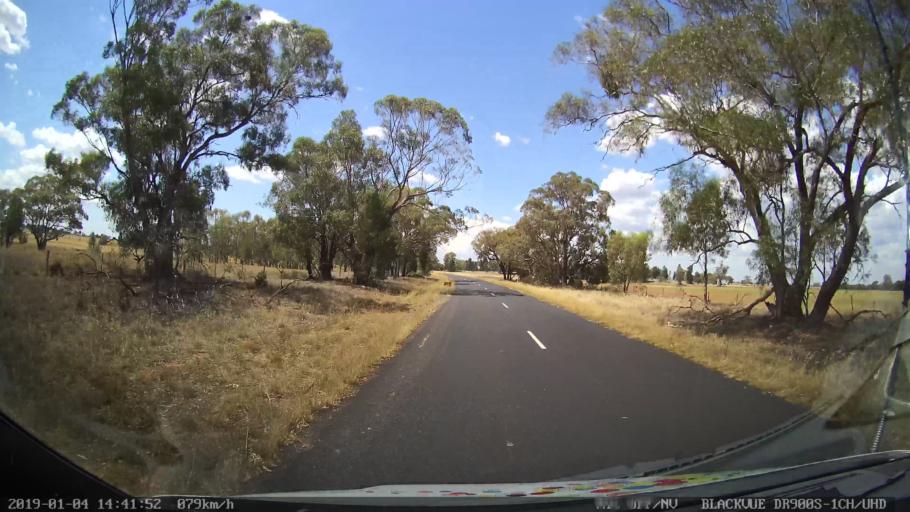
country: AU
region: New South Wales
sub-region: Dubbo Municipality
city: Dubbo
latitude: -32.1346
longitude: 148.6387
